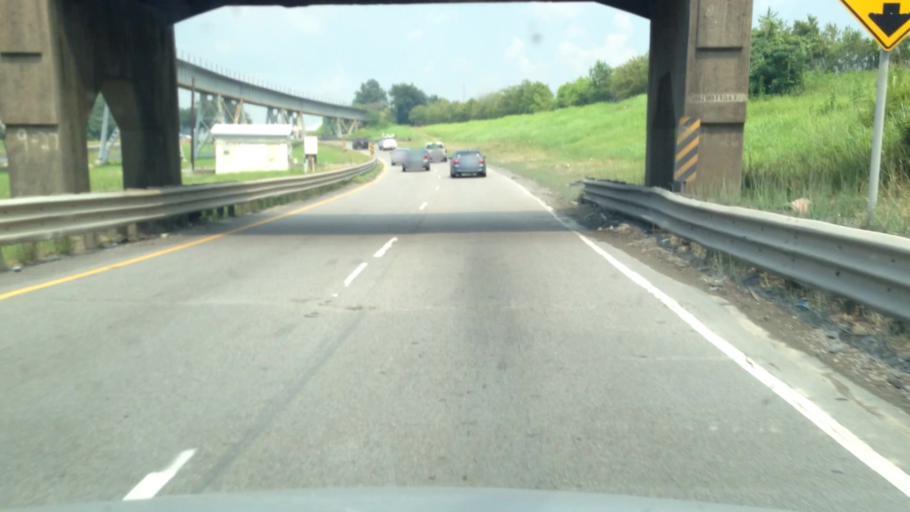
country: US
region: Louisiana
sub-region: West Baton Rouge Parish
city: Port Allen
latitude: 30.5074
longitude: -91.1842
